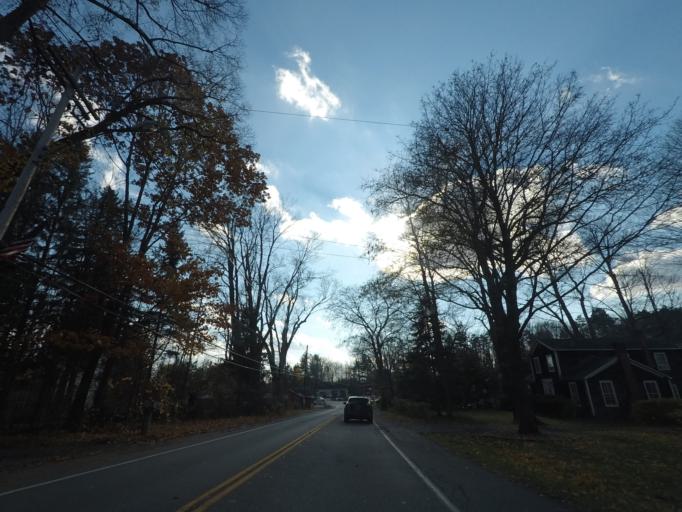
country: US
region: New York
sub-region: Schenectady County
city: East Glenville
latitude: 42.9055
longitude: -73.8966
